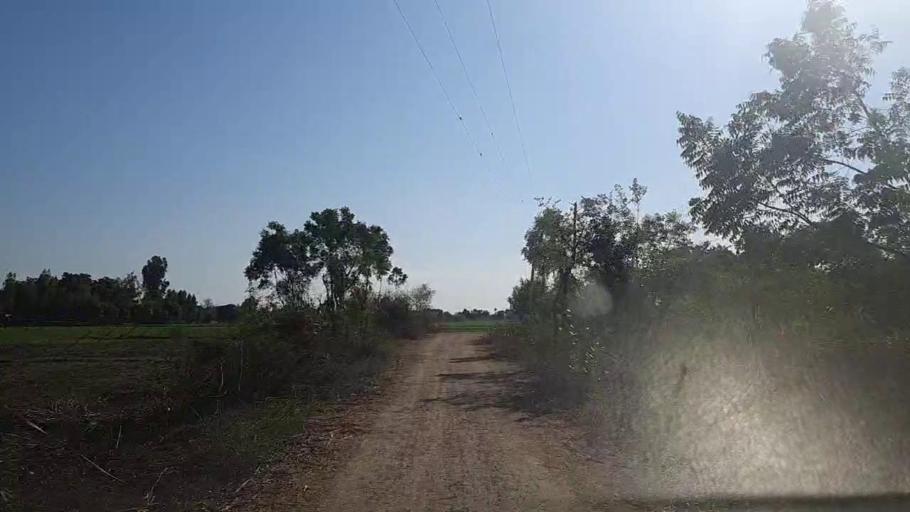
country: PK
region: Sindh
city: Khadro
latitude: 26.2719
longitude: 68.8157
